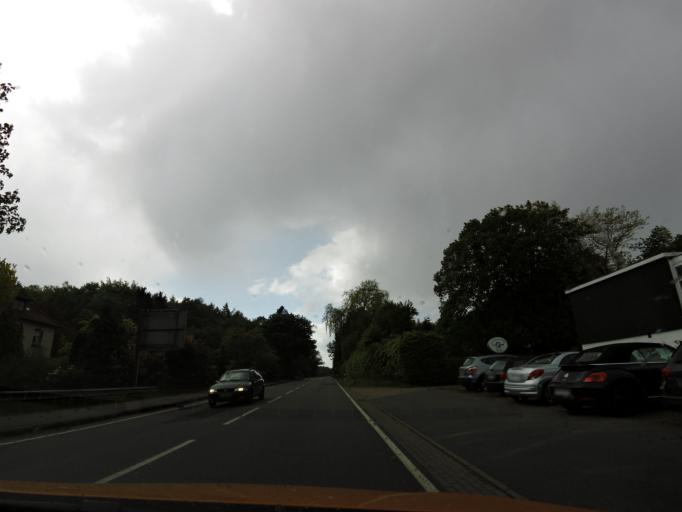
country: DE
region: Lower Saxony
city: Ganderkesee
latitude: 53.0169
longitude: 8.5690
